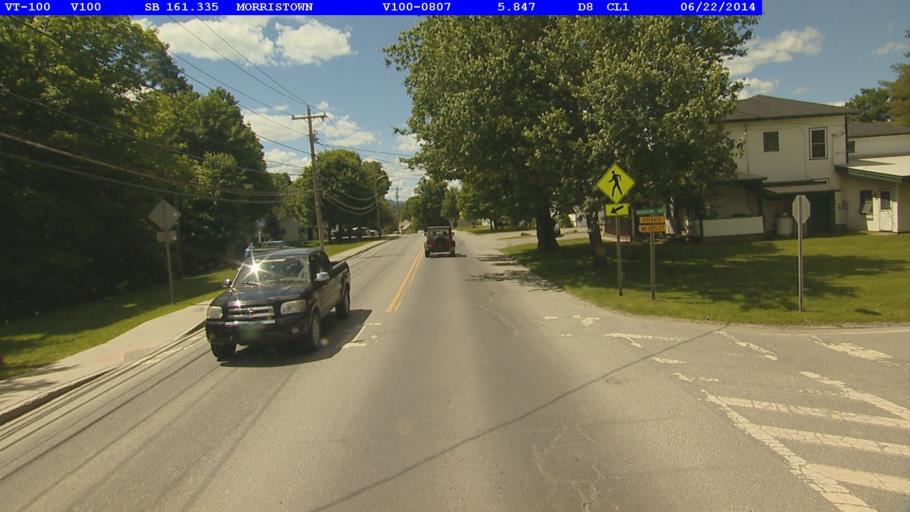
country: US
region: Vermont
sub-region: Lamoille County
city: Morrisville
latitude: 44.5666
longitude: -72.6007
